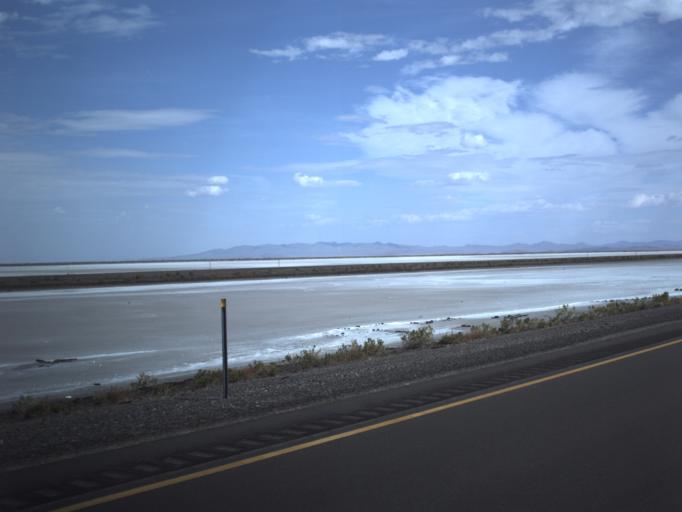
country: US
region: Utah
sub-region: Tooele County
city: Wendover
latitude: 40.7293
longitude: -113.4323
